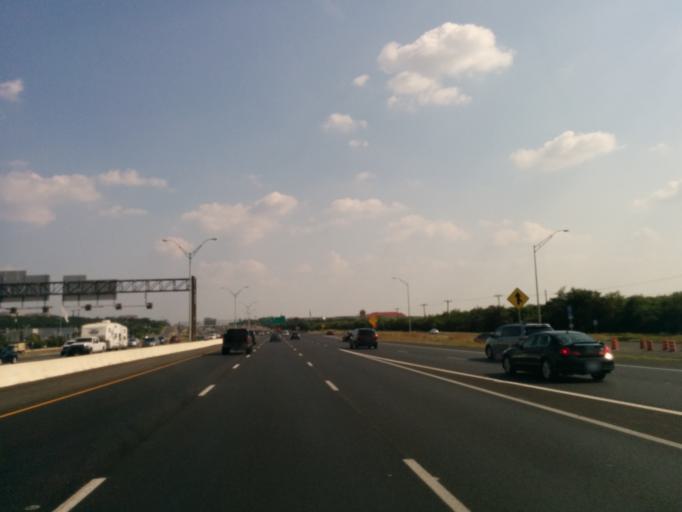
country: US
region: Texas
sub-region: Bexar County
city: Shavano Park
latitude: 29.5868
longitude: -98.5979
